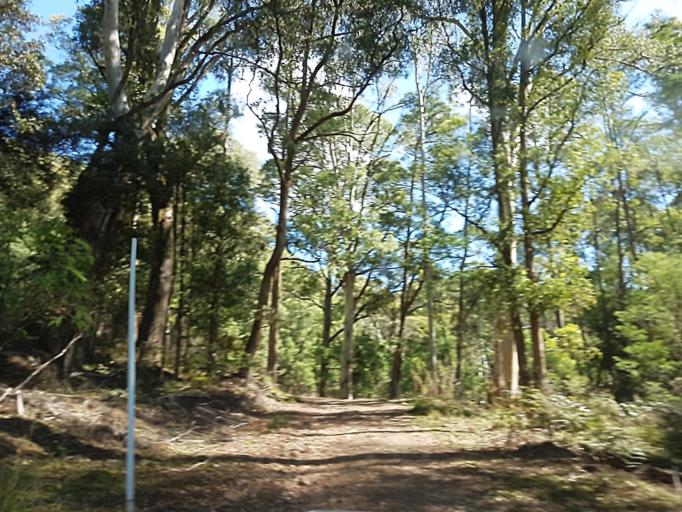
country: AU
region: Victoria
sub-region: Alpine
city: Mount Beauty
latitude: -36.8773
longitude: 147.0466
